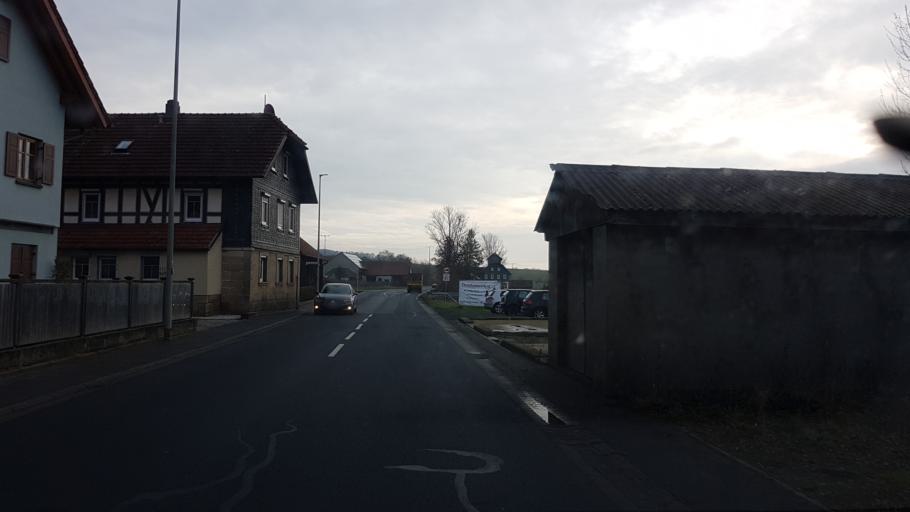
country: DE
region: Bavaria
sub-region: Regierungsbezirk Unterfranken
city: Pfarrweisach
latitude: 50.1598
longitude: 10.7305
